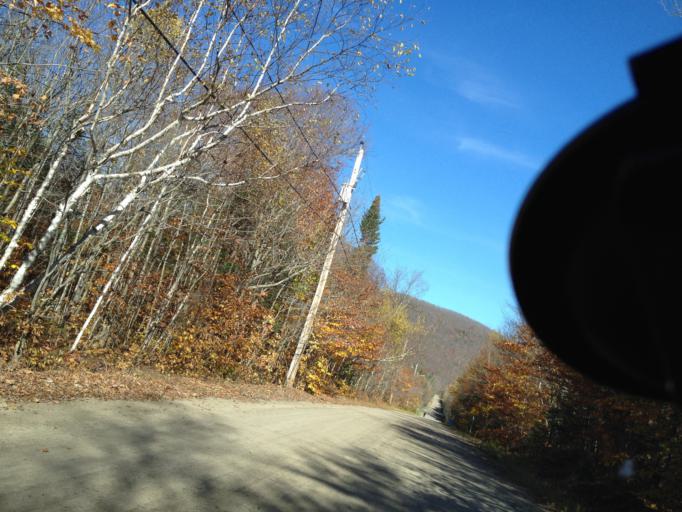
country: CA
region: Quebec
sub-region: Laurentides
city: Val-David
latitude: 46.2912
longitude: -74.1171
